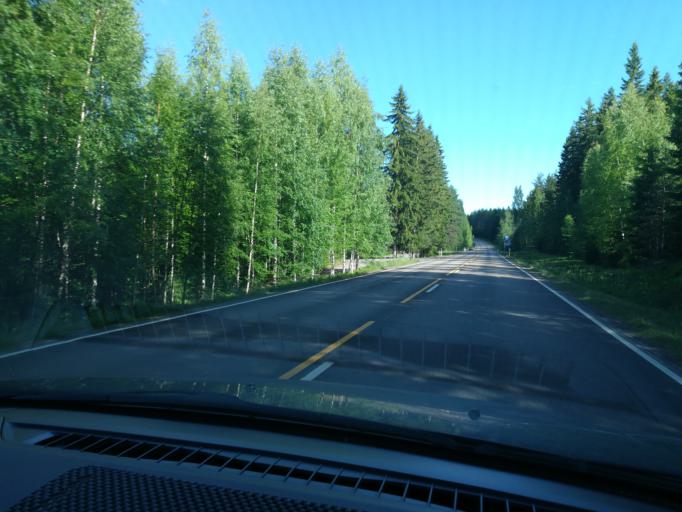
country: FI
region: Southern Savonia
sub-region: Mikkeli
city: Puumala
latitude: 61.5102
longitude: 28.1827
